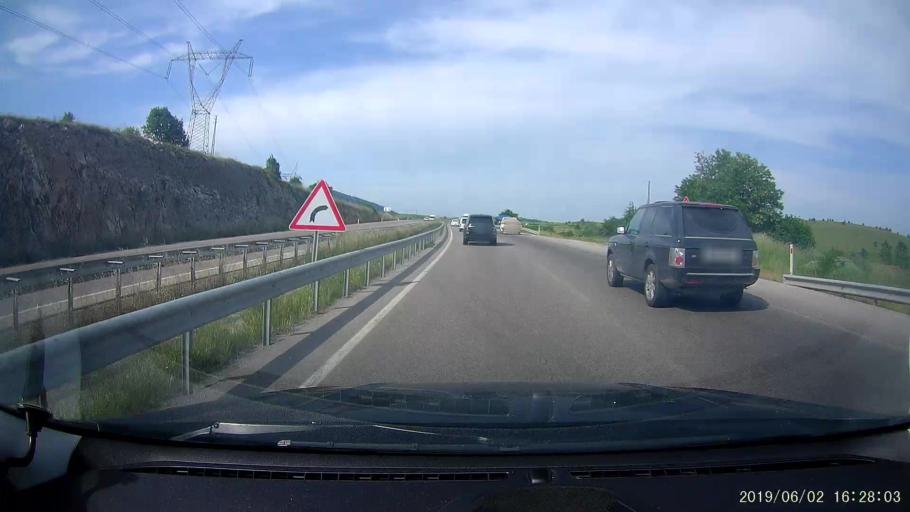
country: TR
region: Samsun
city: Ladik
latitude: 41.0041
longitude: 35.8399
